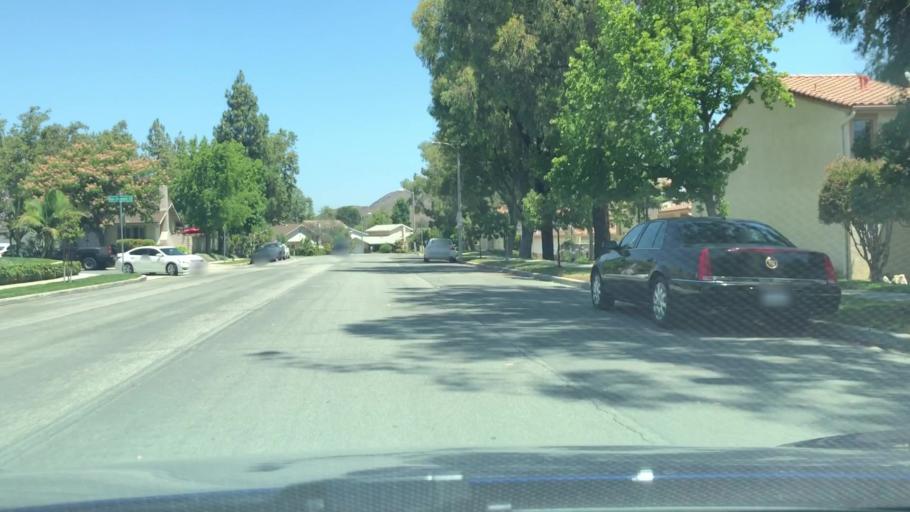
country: US
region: California
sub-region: Ventura County
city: Casa Conejo
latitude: 34.1811
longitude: -118.9556
